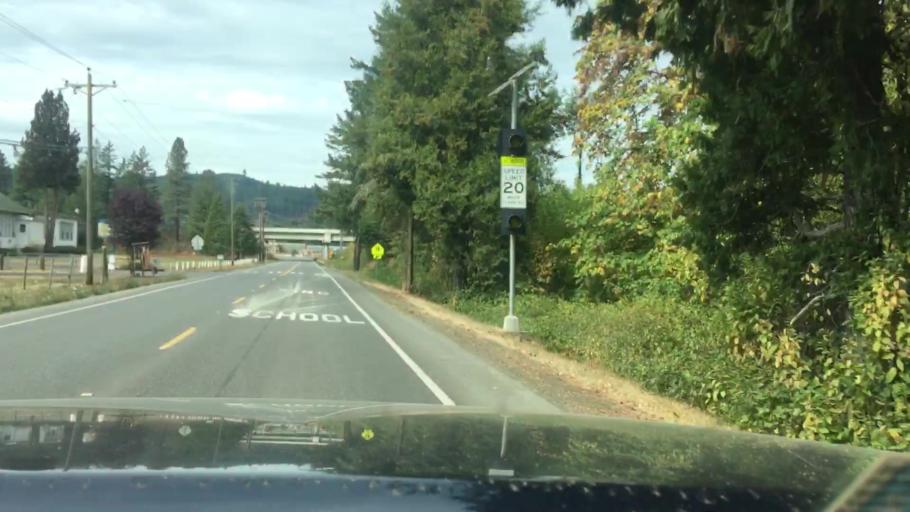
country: US
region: Oregon
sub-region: Lane County
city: Cottage Grove
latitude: 43.7641
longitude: -123.0703
